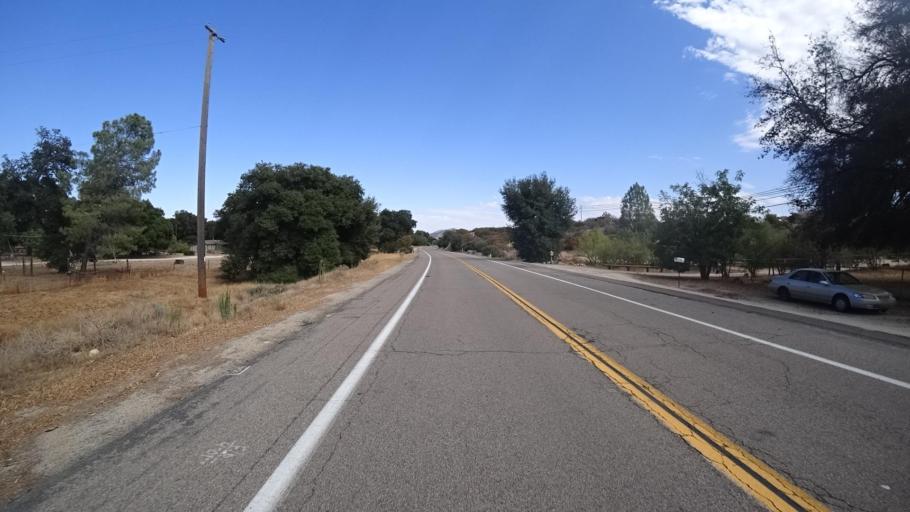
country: MX
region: Baja California
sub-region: Tecate
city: Cereso del Hongo
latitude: 32.6658
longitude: -116.2813
